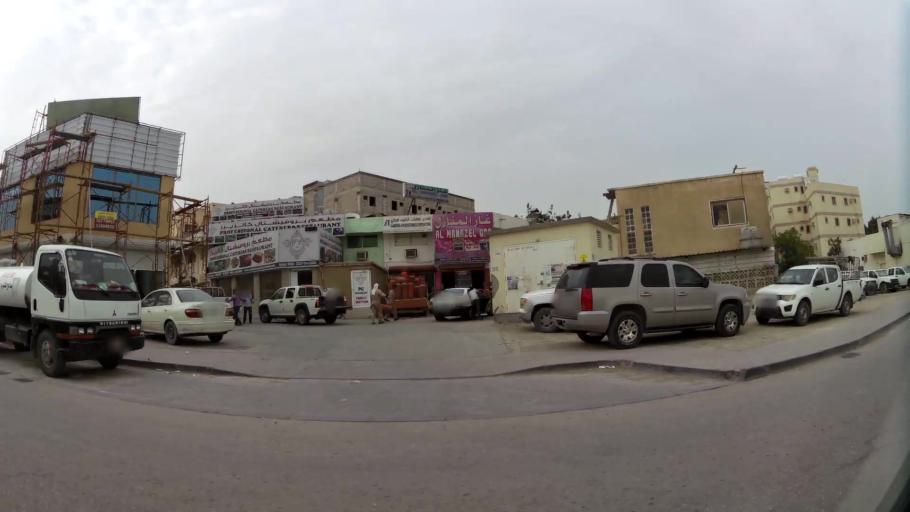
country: BH
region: Northern
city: Ar Rifa'
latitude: 26.1170
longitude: 50.5704
